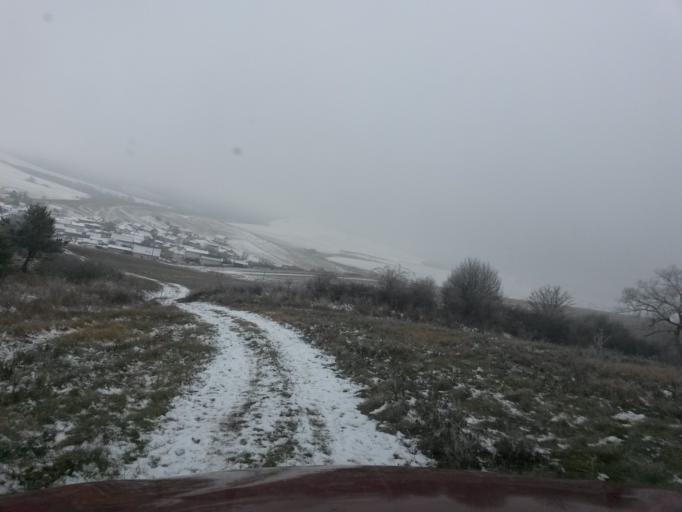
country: SK
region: Kosicky
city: Krompachy
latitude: 48.9685
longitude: 20.9764
